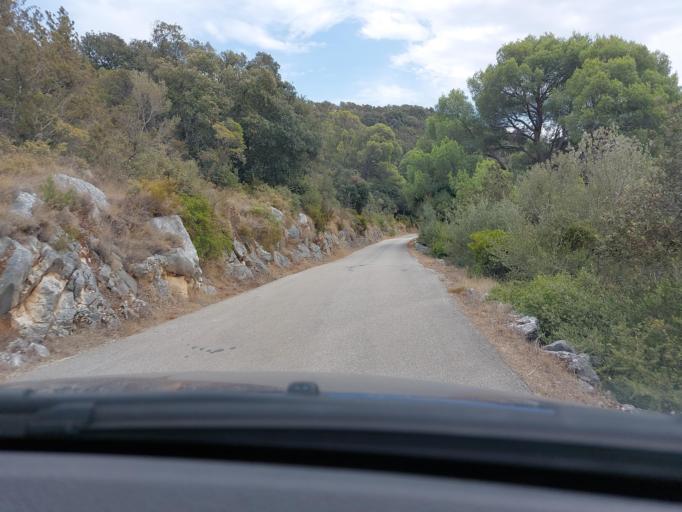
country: HR
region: Dubrovacko-Neretvanska
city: Smokvica
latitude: 42.7596
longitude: 16.9167
